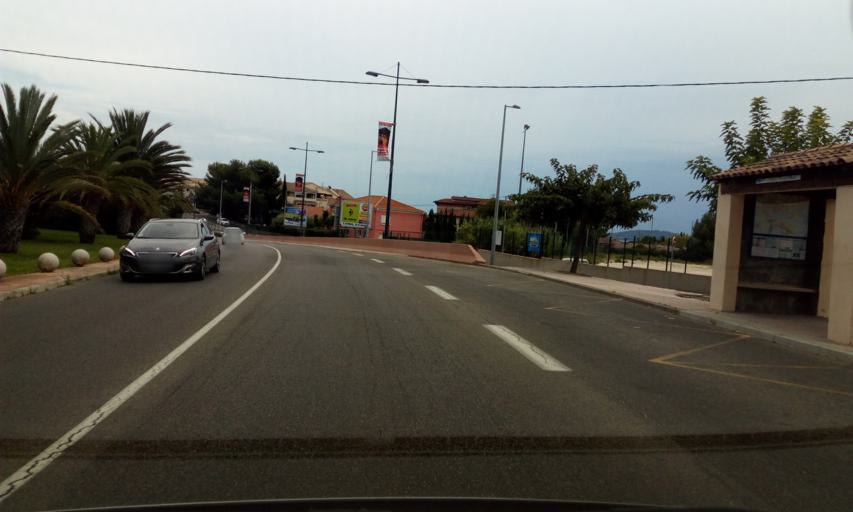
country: FR
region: Provence-Alpes-Cote d'Azur
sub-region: Departement du Var
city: Carqueiranne
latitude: 43.0936
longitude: 6.0718
